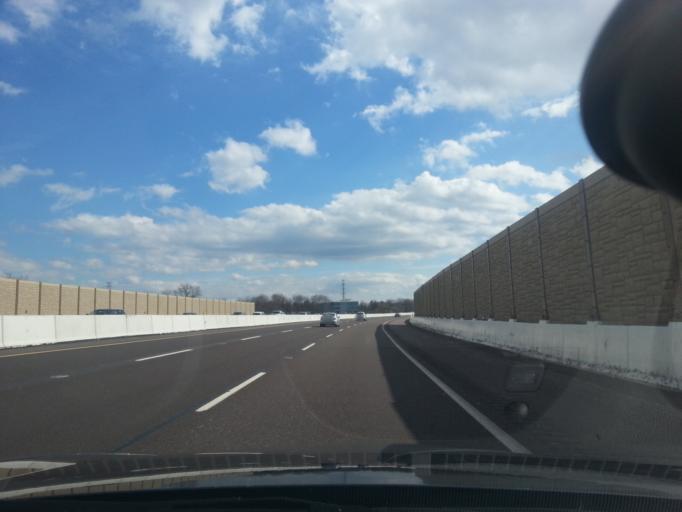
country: US
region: Pennsylvania
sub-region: Montgomery County
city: Blue Bell
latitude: 40.1532
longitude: -75.2933
